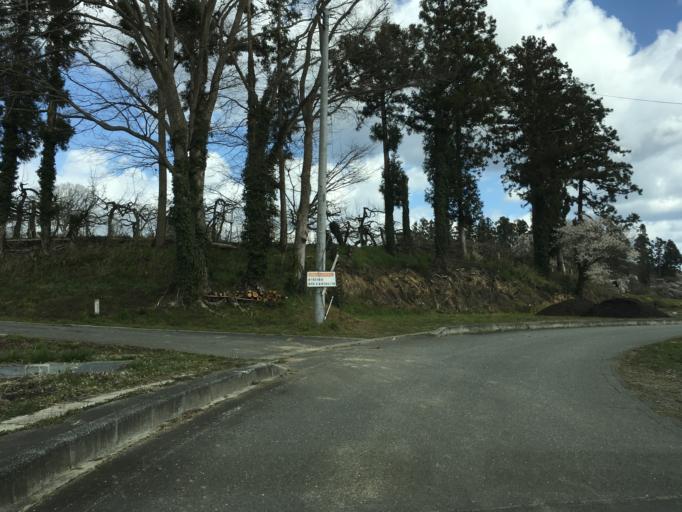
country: JP
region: Iwate
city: Ichinoseki
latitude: 38.7512
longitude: 141.2631
